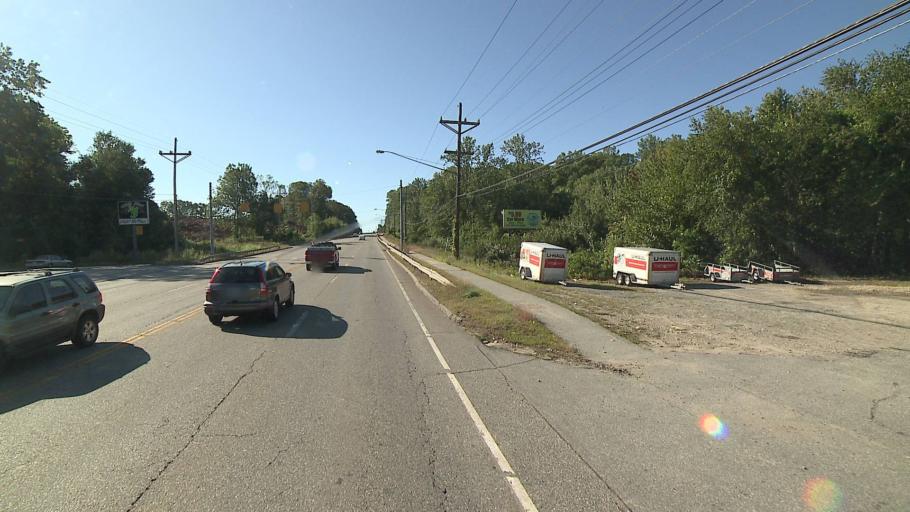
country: US
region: Connecticut
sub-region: New London County
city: Conning Towers-Nautilus Park
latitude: 41.3867
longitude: -72.0788
